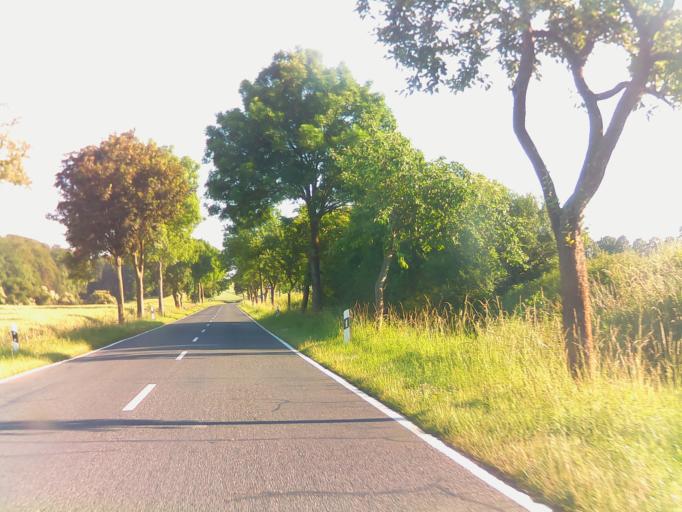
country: DE
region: Lower Saxony
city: Baddeckenstedt
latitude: 52.0829
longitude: 10.2008
